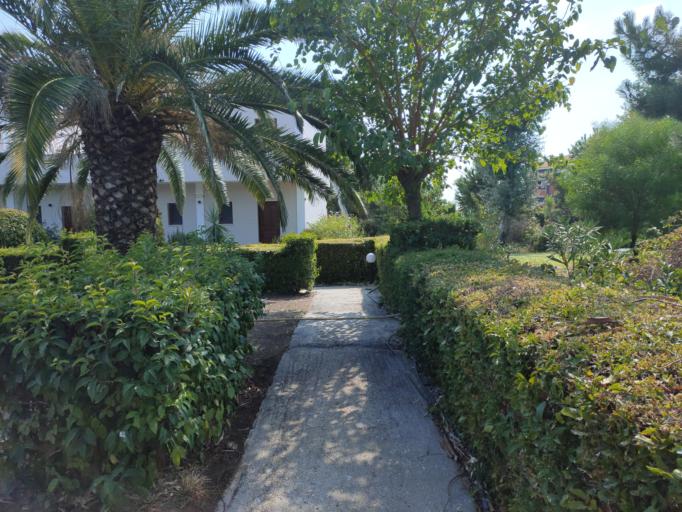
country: GR
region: North Aegean
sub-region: Nomos Lesvou
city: Kalloni
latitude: 39.2094
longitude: 26.2059
